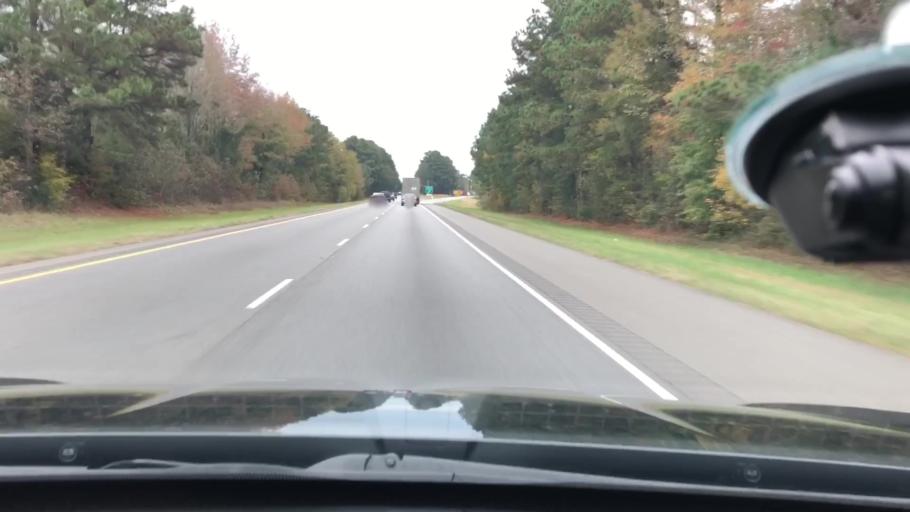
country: US
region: Arkansas
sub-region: Hempstead County
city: Hope
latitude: 33.6475
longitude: -93.6781
